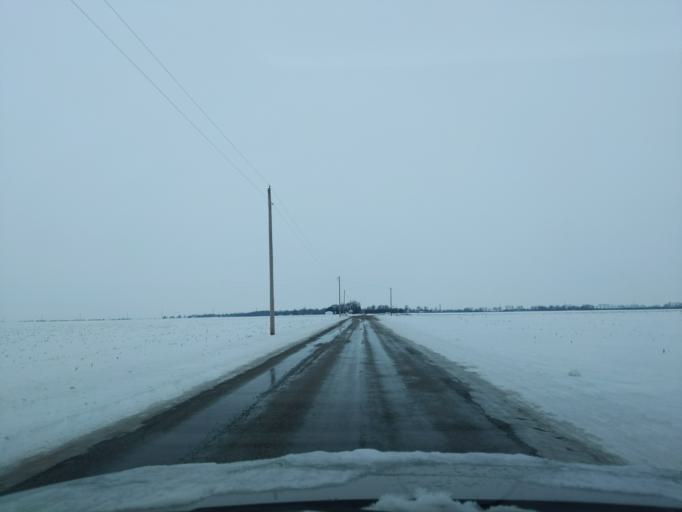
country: US
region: Indiana
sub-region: Benton County
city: Otterbein
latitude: 40.4664
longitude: -87.0932
